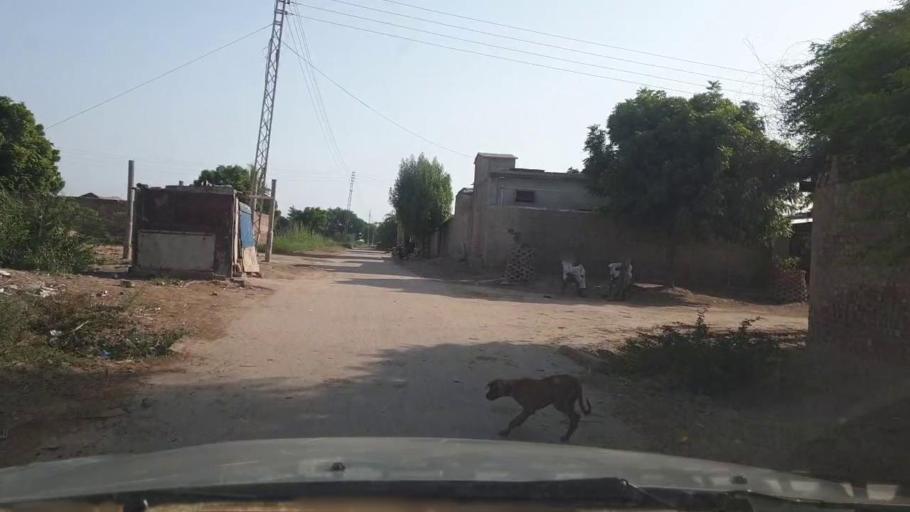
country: PK
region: Sindh
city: Tando Ghulam Ali
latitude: 25.2089
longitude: 68.9640
